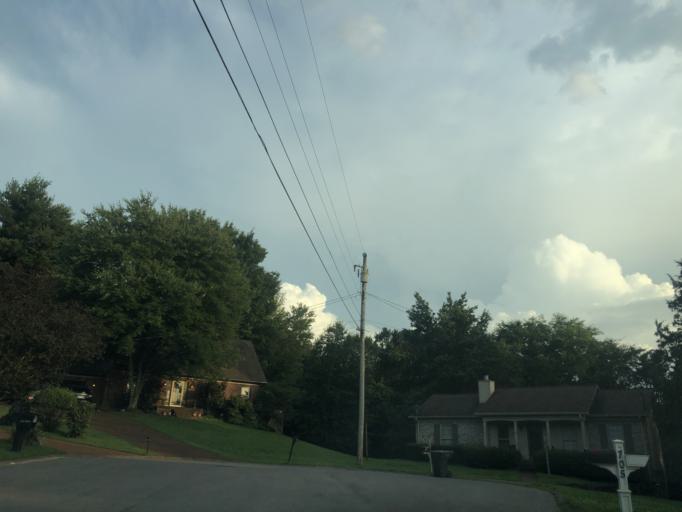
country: US
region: Tennessee
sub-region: Davidson County
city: Lakewood
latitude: 36.1400
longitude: -86.6312
